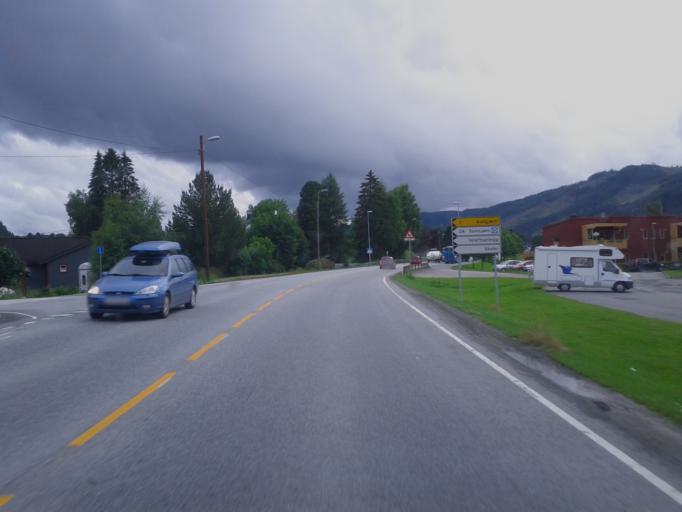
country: NO
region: Sor-Trondelag
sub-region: Melhus
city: Lundamo
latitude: 63.1529
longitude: 10.2893
